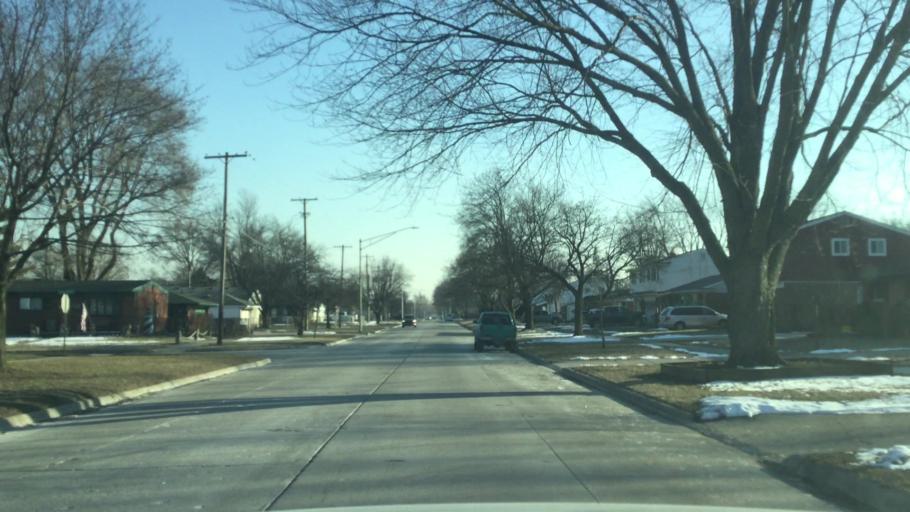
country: US
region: Michigan
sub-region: Wayne County
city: Westland
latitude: 42.3162
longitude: -83.3792
